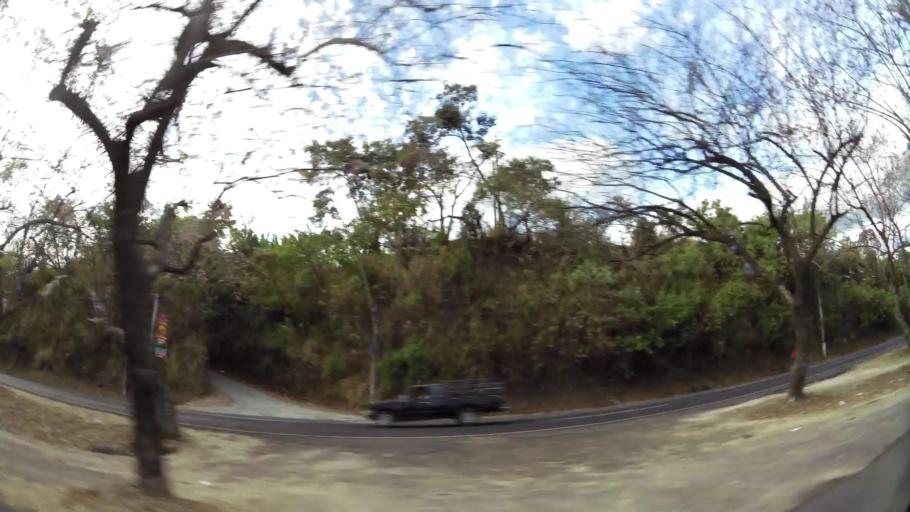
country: SV
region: San Vicente
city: San Sebastian
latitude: 13.7289
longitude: -88.8774
